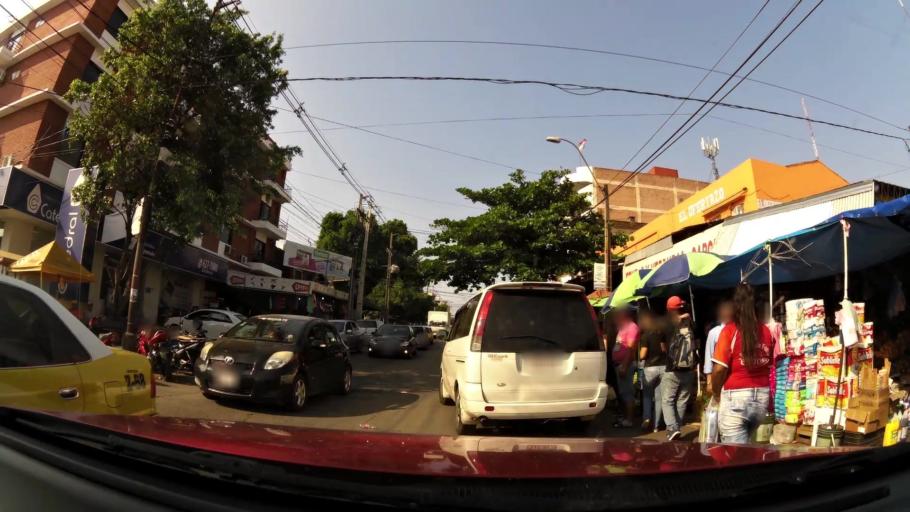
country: PY
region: Asuncion
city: Asuncion
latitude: -25.2974
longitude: -57.6251
